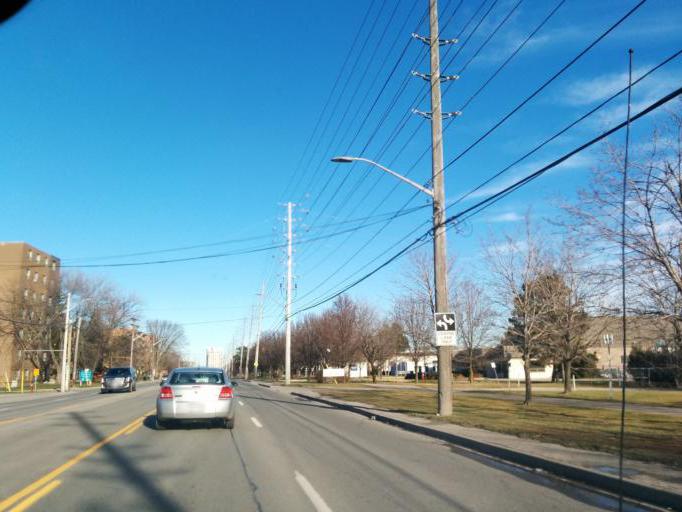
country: CA
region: Ontario
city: Etobicoke
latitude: 43.5803
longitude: -79.5551
